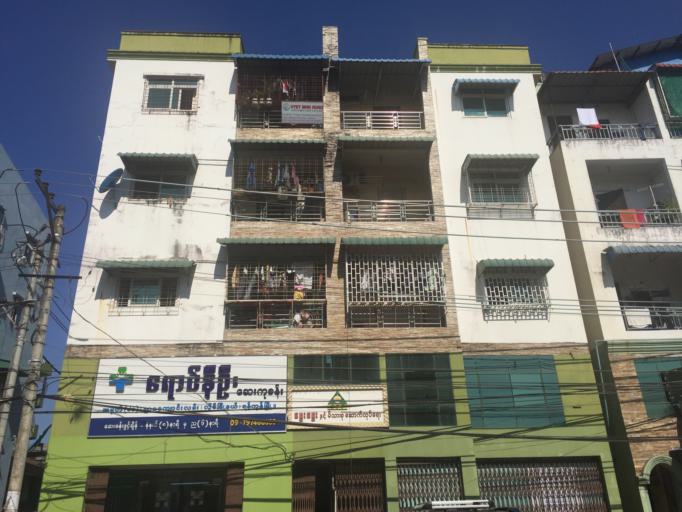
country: MM
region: Yangon
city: Yangon
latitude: 16.8352
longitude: 96.1268
